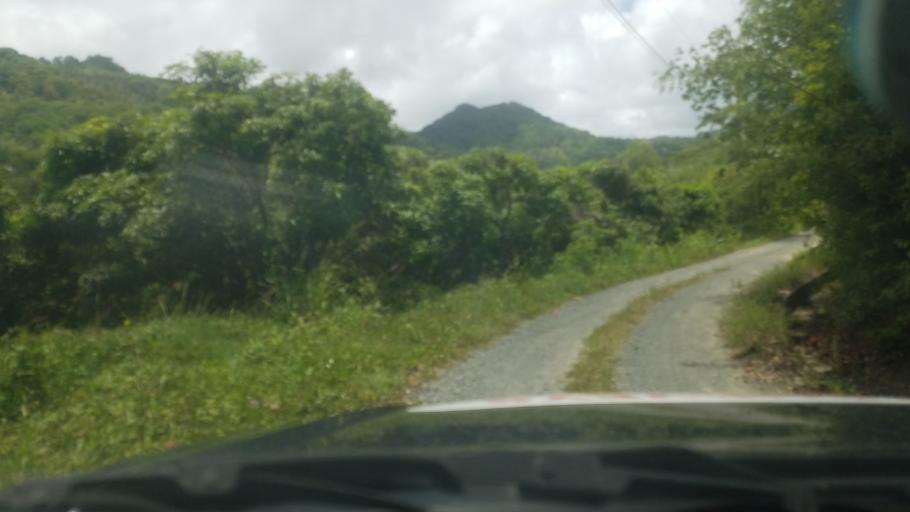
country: LC
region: Praslin
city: Praslin
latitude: 13.8663
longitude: -60.9067
